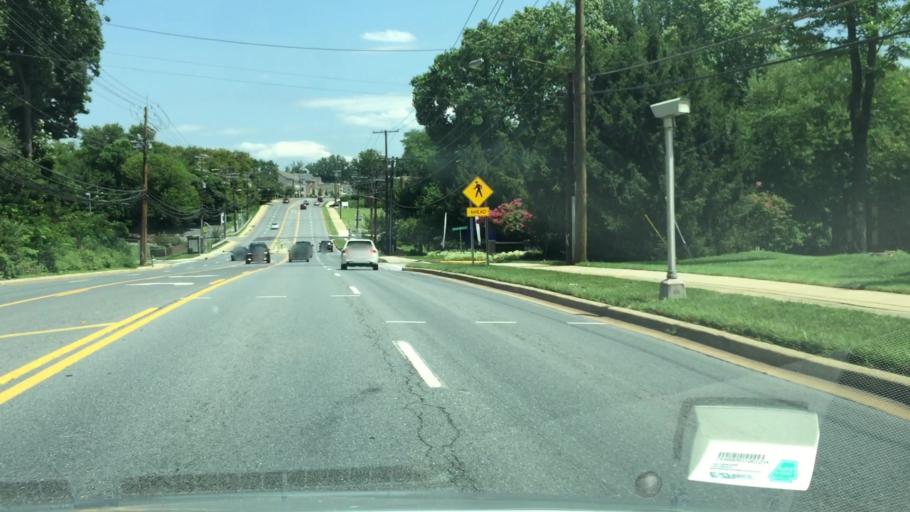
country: US
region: Maryland
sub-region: Montgomery County
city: Leisure World
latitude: 39.0913
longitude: -77.0673
